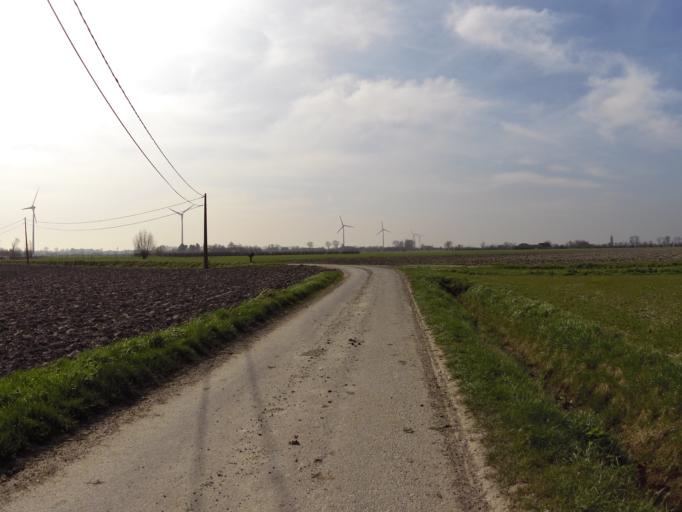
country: BE
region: Flanders
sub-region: Provincie West-Vlaanderen
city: Oudenburg
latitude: 51.1766
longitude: 2.9779
